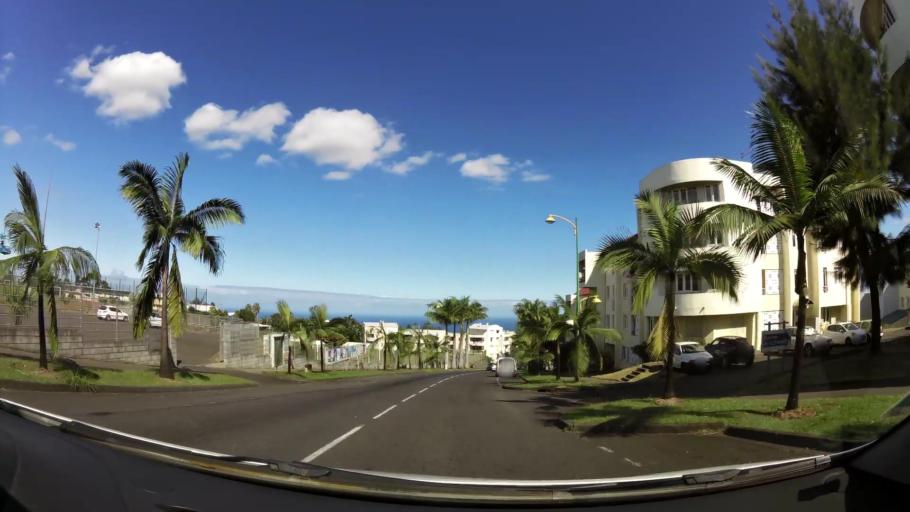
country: RE
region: Reunion
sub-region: Reunion
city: Le Tampon
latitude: -21.2753
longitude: 55.5055
